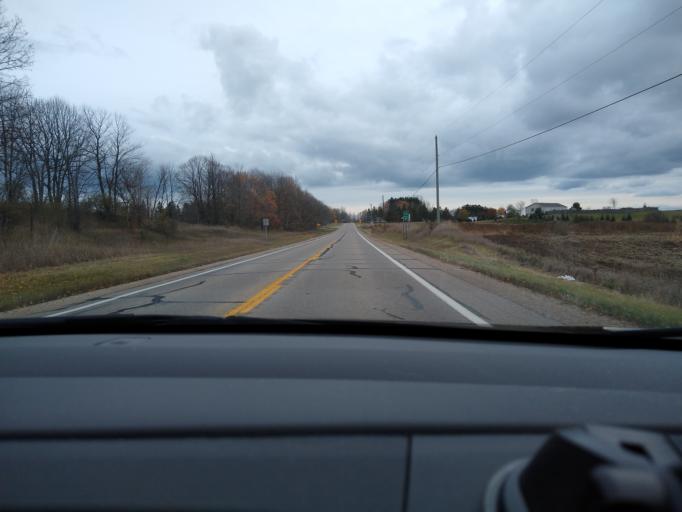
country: US
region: Michigan
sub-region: Delta County
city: Escanaba
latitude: 45.7412
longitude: -87.2694
